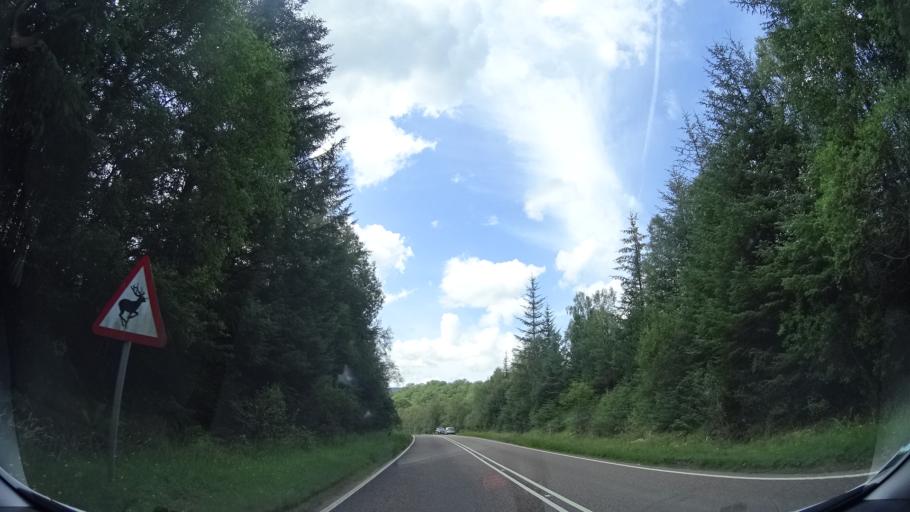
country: GB
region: Scotland
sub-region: Highland
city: Fort William
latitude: 56.8647
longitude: -5.3907
